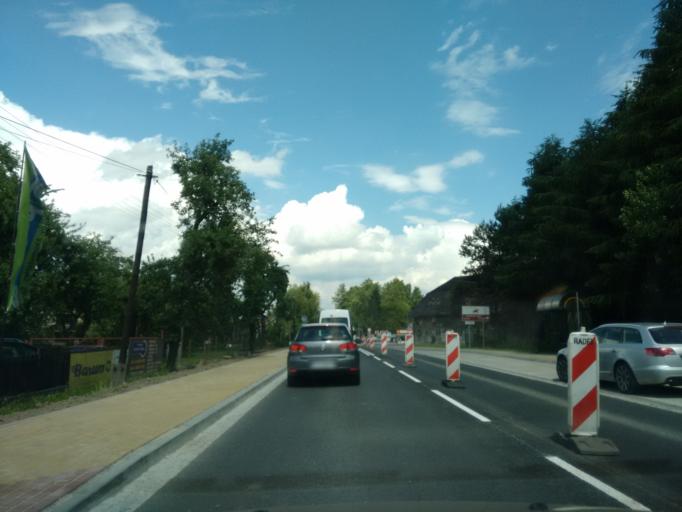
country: PL
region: Silesian Voivodeship
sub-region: Powiat cieszynski
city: Pruchna
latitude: 49.8644
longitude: 18.6814
